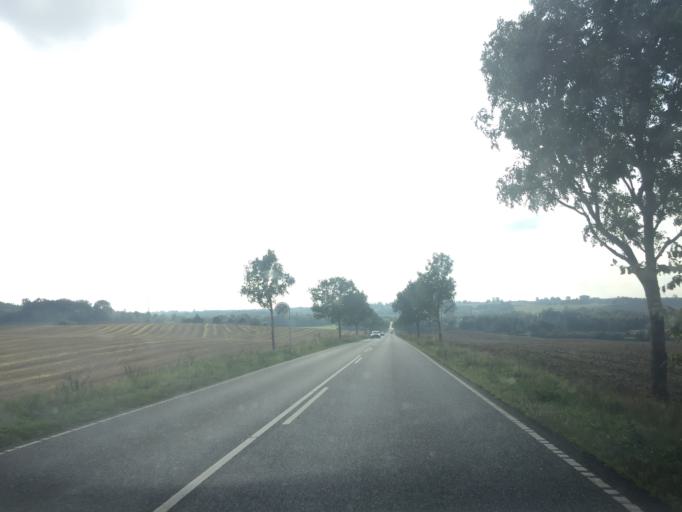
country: DK
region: Zealand
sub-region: Holbaek Kommune
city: Tollose
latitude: 55.6429
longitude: 11.8036
